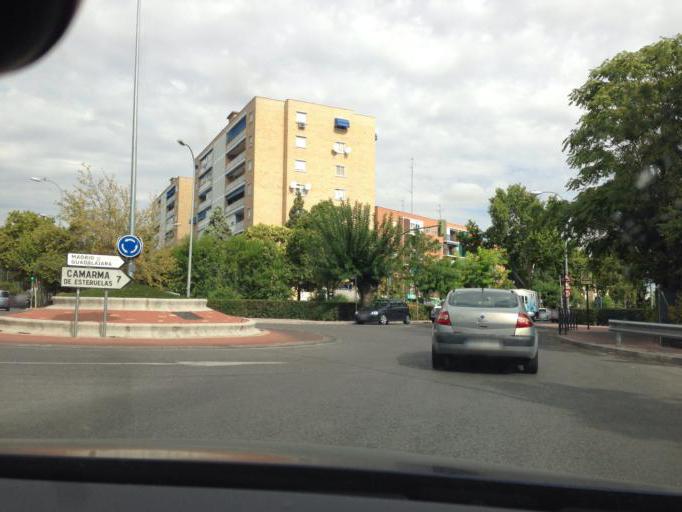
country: ES
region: Madrid
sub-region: Provincia de Madrid
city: Alcala de Henares
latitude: 40.4913
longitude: -3.3775
